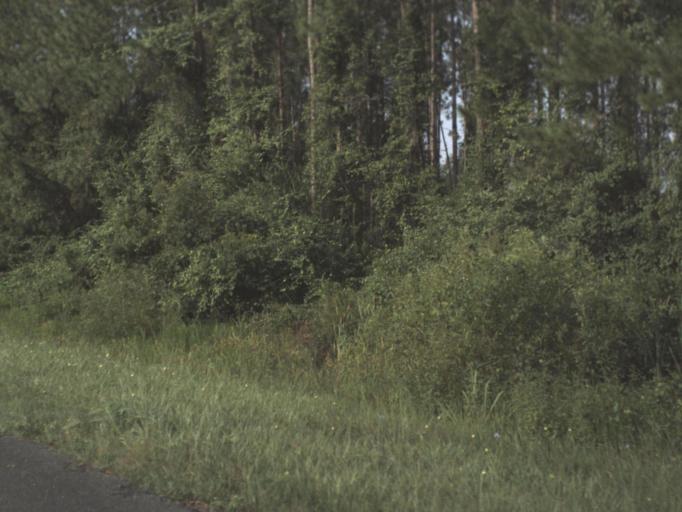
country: US
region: Florida
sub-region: Taylor County
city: Perry
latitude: 30.2336
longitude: -83.6180
